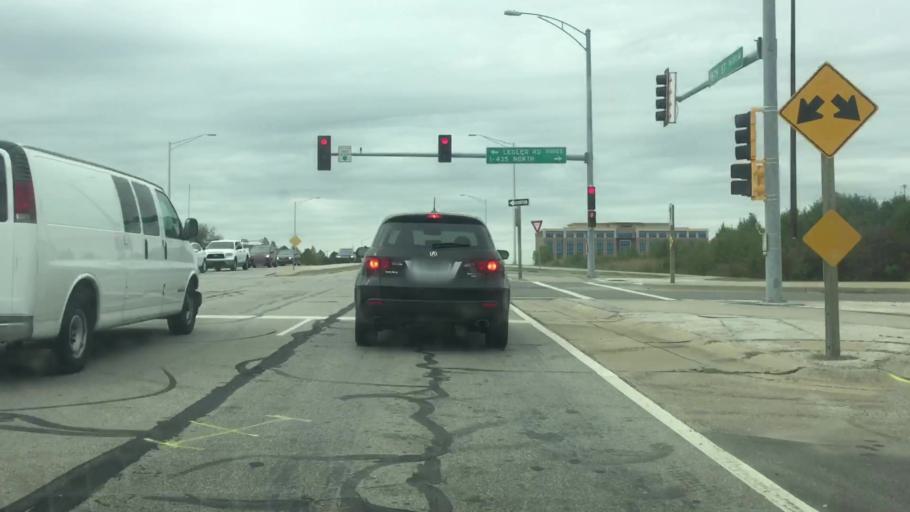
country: US
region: Kansas
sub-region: Johnson County
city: Lenexa
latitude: 38.9566
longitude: -94.7722
